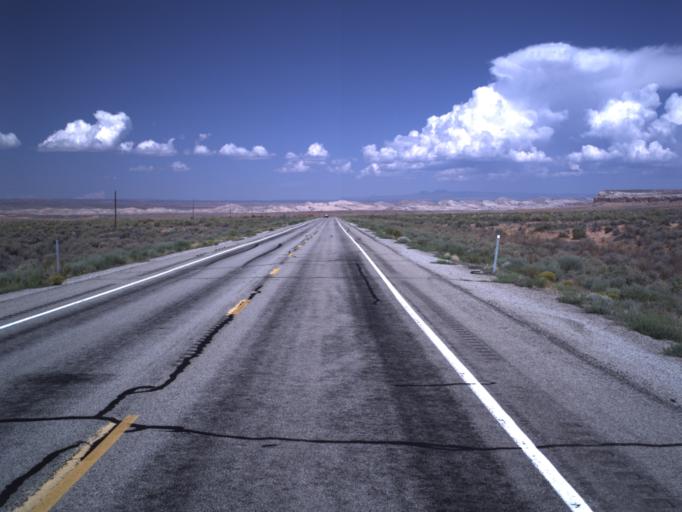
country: US
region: Utah
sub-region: San Juan County
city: Blanding
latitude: 37.1889
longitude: -109.5945
